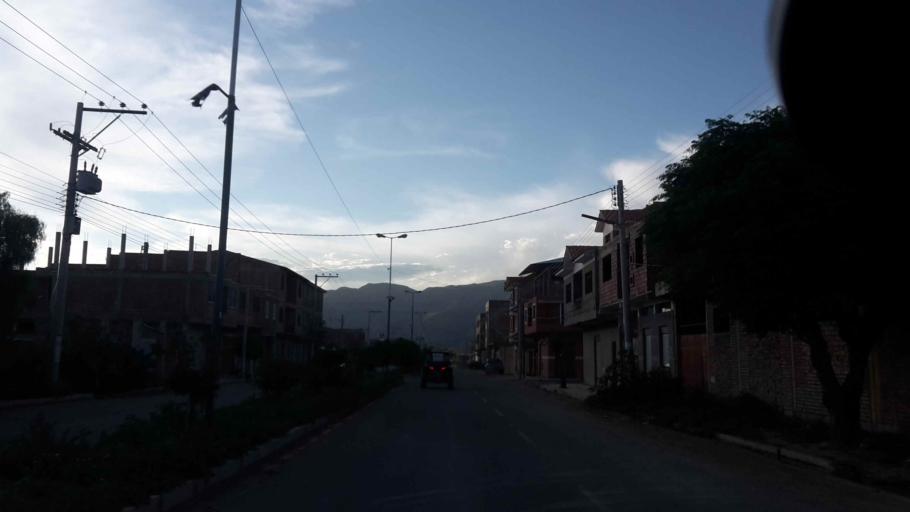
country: BO
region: Cochabamba
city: Punata
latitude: -17.5418
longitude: -65.8306
